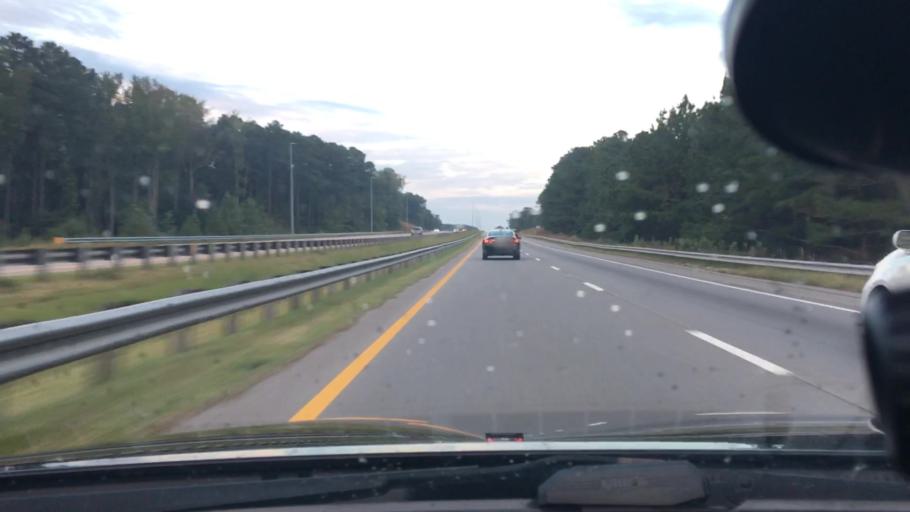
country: US
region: North Carolina
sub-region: Wake County
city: Apex
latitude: 35.6901
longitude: -78.8859
